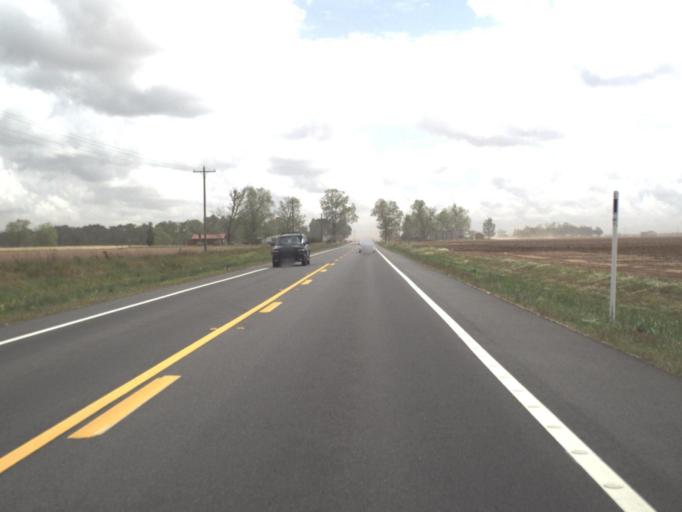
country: US
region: Florida
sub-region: Escambia County
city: Century
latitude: 30.9099
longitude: -87.1687
